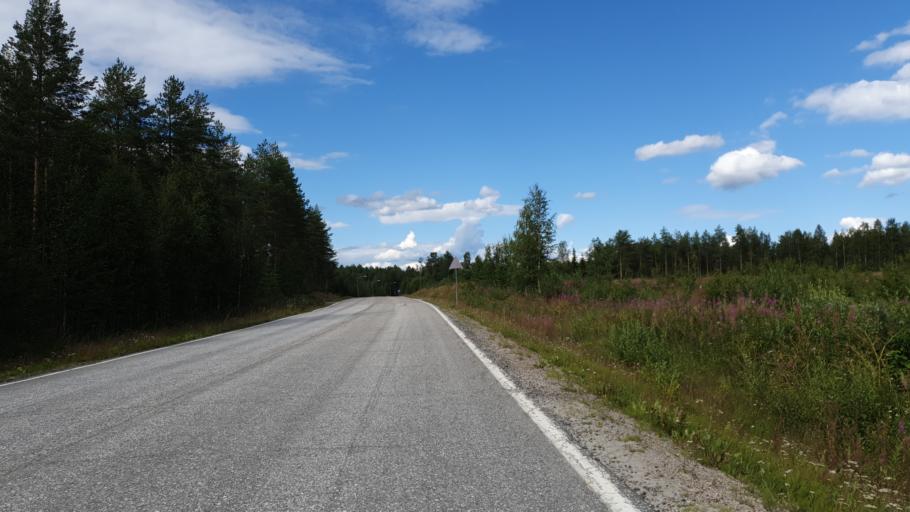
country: FI
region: Kainuu
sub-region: Kehys-Kainuu
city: Kuhmo
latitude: 64.1142
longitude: 29.5277
